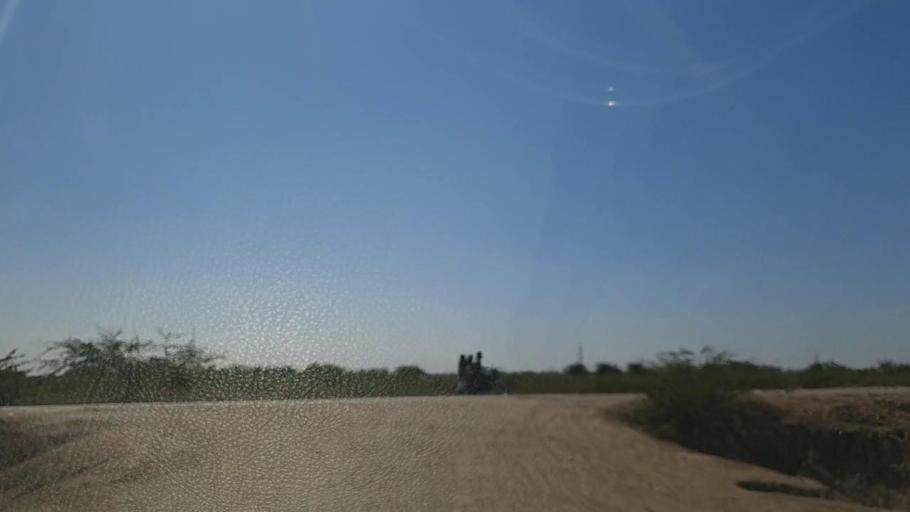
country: PK
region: Sindh
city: Samaro
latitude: 25.2992
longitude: 69.4839
